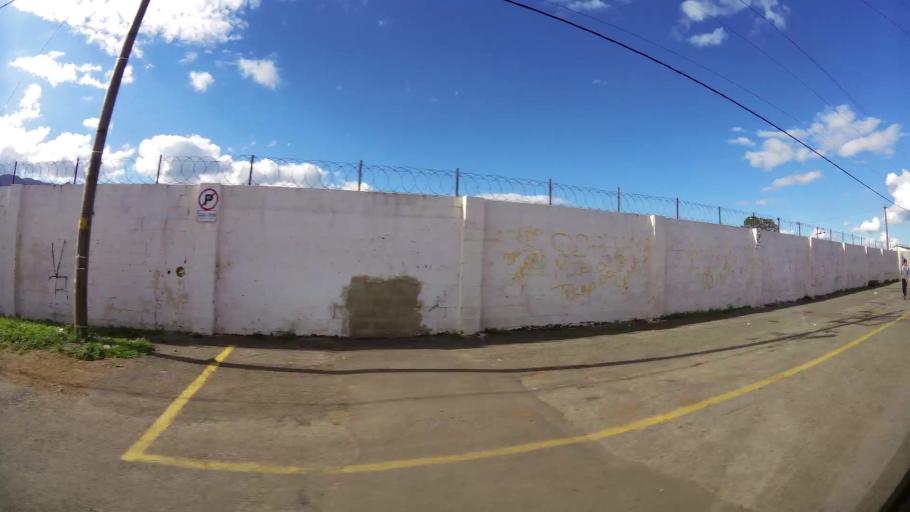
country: ZA
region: Western Cape
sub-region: Overberg District Municipality
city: Swellendam
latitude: -34.0399
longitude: 20.4437
